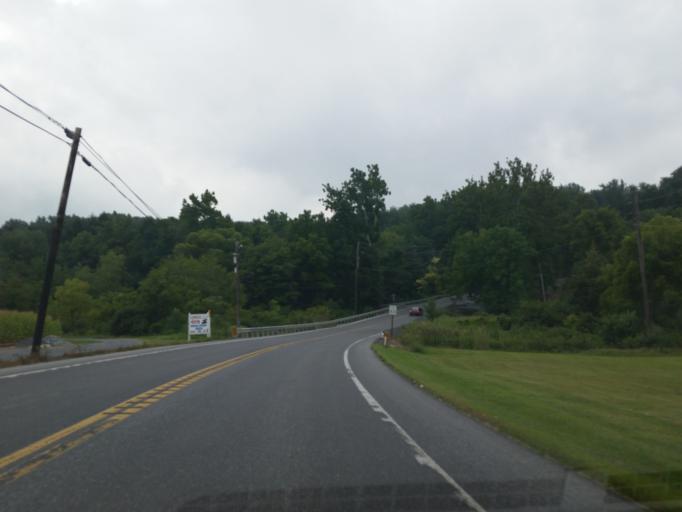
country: US
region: Pennsylvania
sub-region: Lancaster County
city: Brickerville
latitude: 40.2762
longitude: -76.2958
